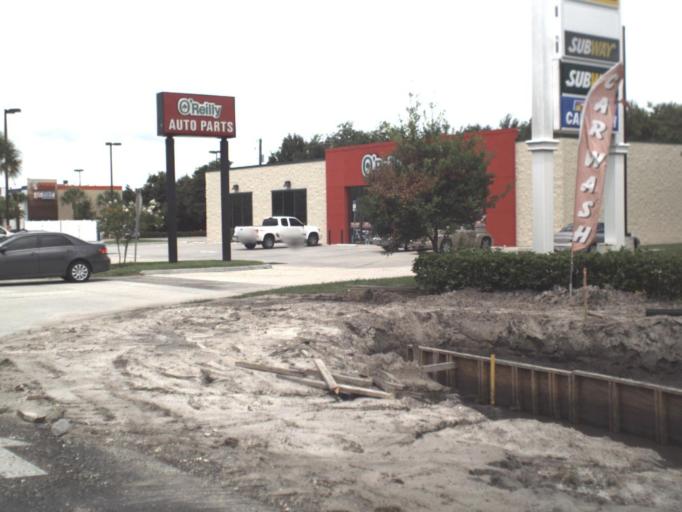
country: US
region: Florida
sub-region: Hillsborough County
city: Egypt Lake-Leto
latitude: 27.9963
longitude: -82.5153
